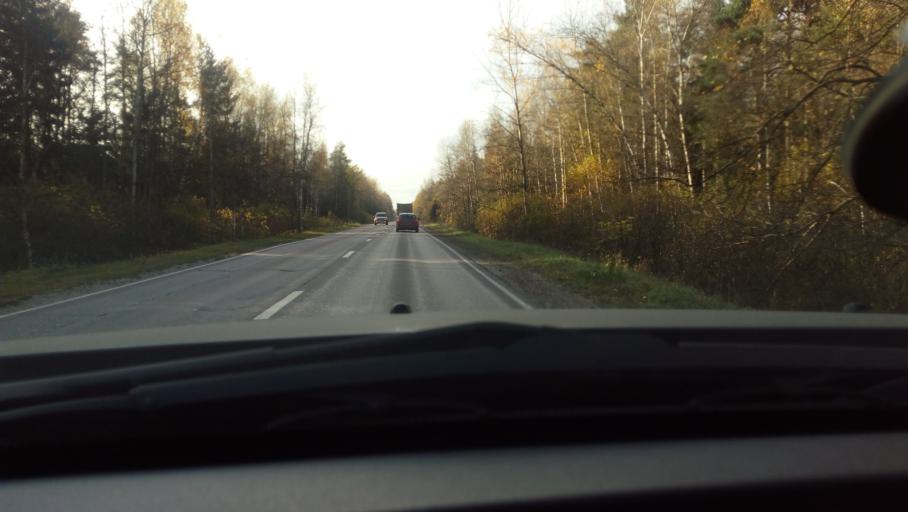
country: RU
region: Moskovskaya
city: Fryazevo
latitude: 55.7056
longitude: 38.4482
